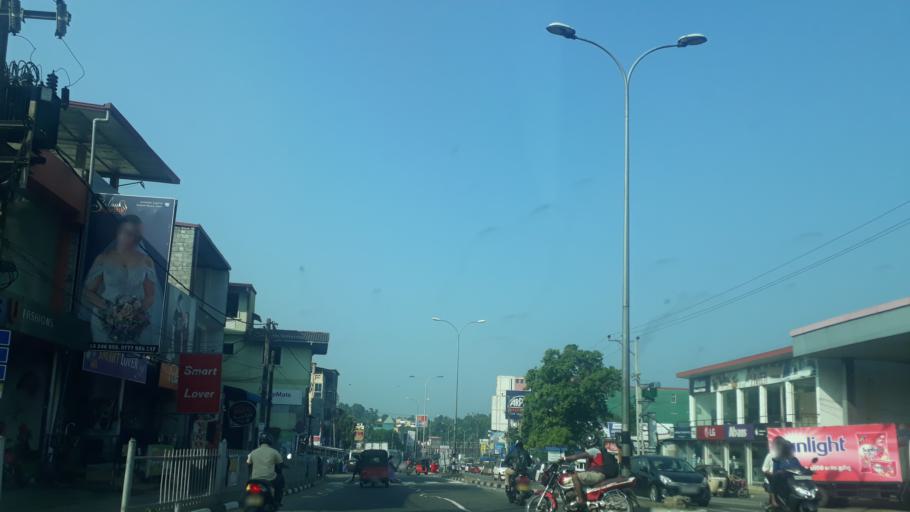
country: LK
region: Western
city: Kelaniya
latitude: 7.0017
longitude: 79.9509
